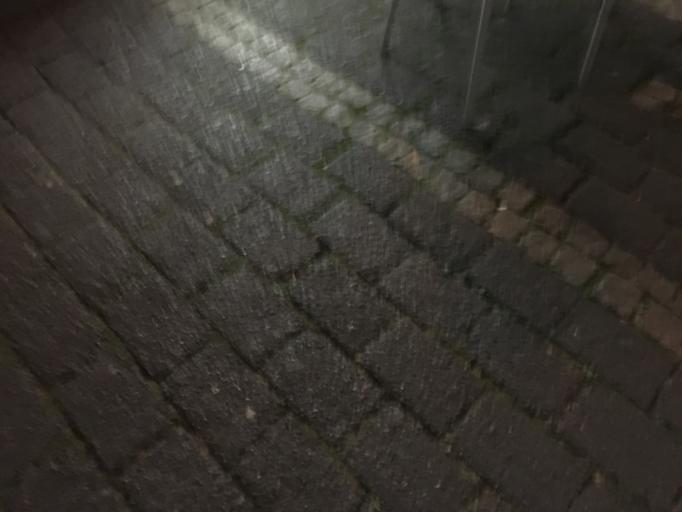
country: DE
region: Hesse
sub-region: Regierungsbezirk Giessen
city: Marburg an der Lahn
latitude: 50.8111
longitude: 8.7702
